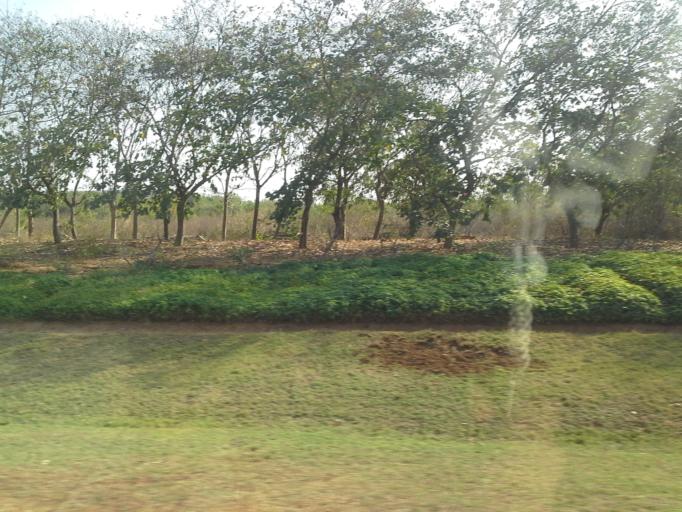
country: IN
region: Telangana
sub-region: Rangareddi
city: Balapur
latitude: 17.2405
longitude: 78.4173
